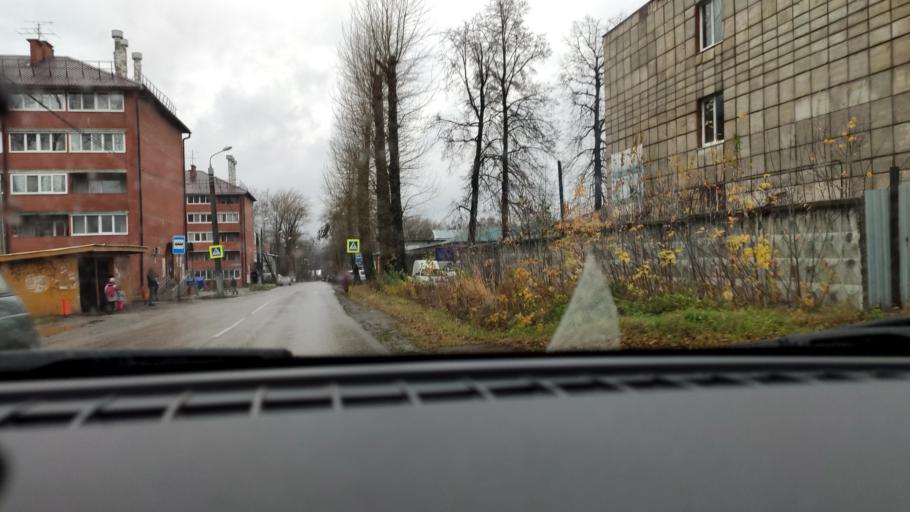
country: RU
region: Perm
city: Perm
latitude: 58.0963
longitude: 56.3717
